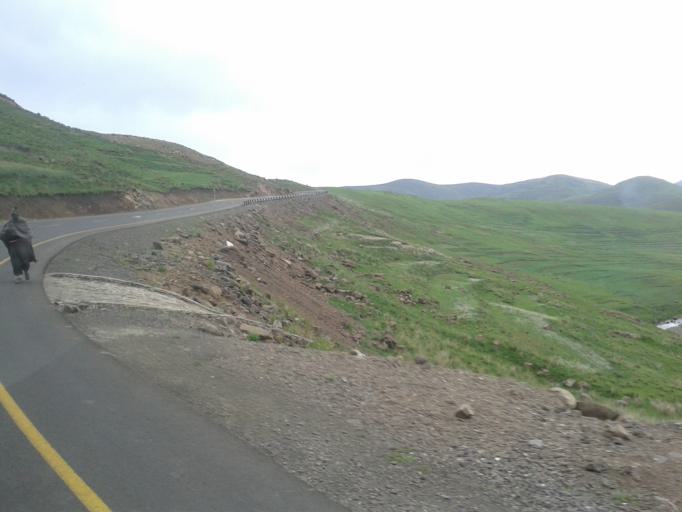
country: LS
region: Maseru
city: Nako
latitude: -29.7865
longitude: 28.0217
